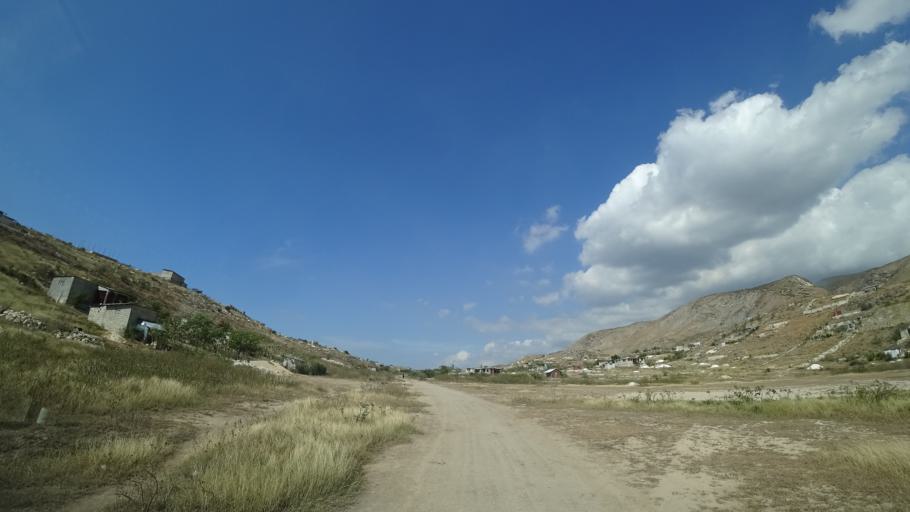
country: HT
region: Ouest
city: Croix des Bouquets
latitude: 18.6760
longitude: -72.2909
